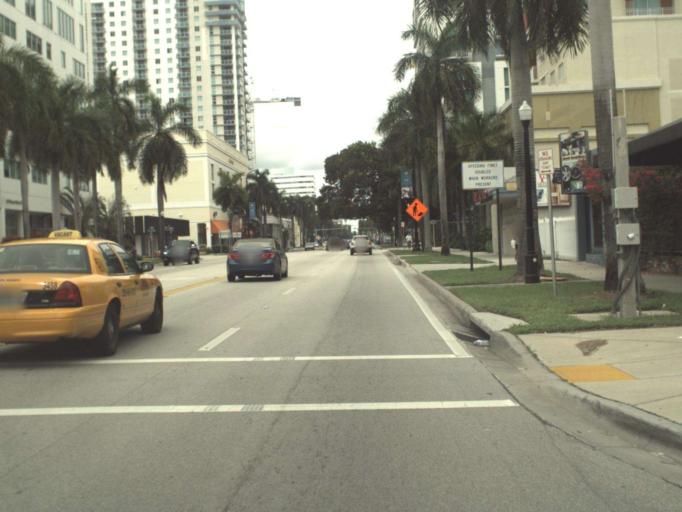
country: US
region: Florida
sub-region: Miami-Dade County
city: Miami
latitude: 25.7982
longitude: -80.1890
